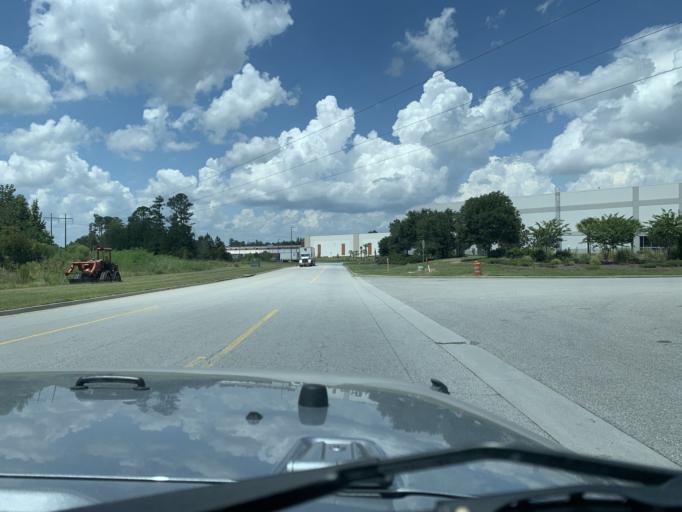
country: US
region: Georgia
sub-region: Chatham County
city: Pooler
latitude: 32.1053
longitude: -81.2731
